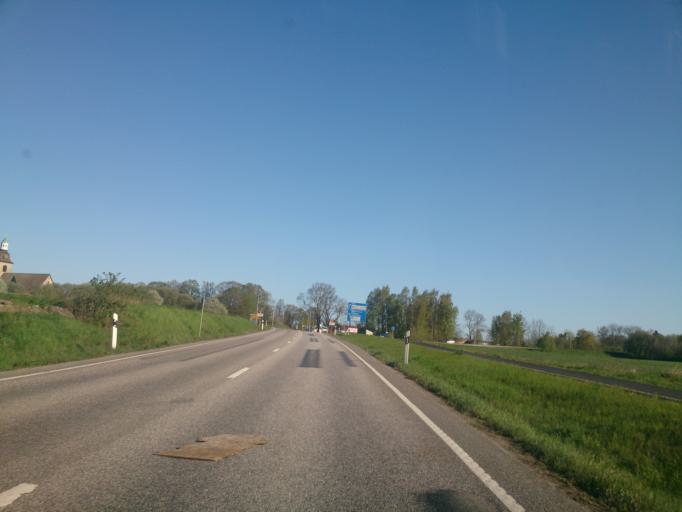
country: SE
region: OEstergoetland
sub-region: Linkopings Kommun
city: Berg
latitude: 58.4801
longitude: 15.5227
